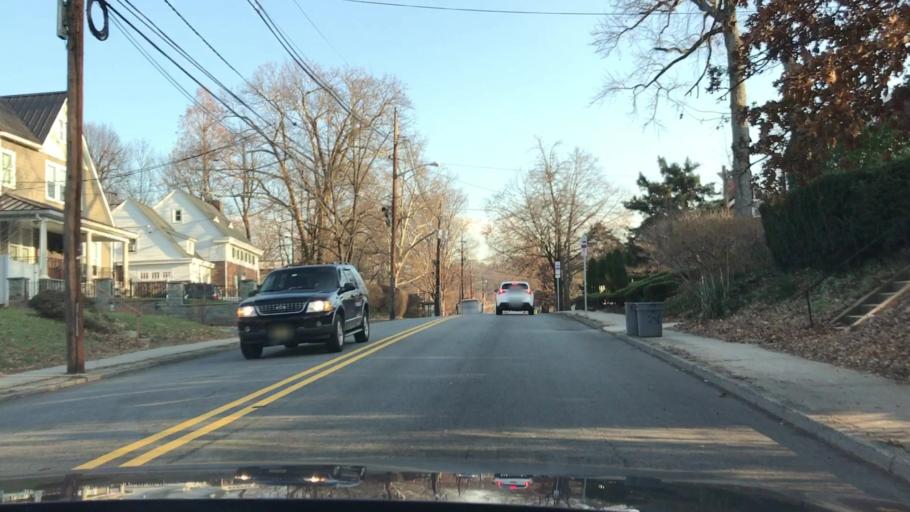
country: US
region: New Jersey
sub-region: Bergen County
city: Leonia
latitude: 40.8630
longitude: -73.9901
